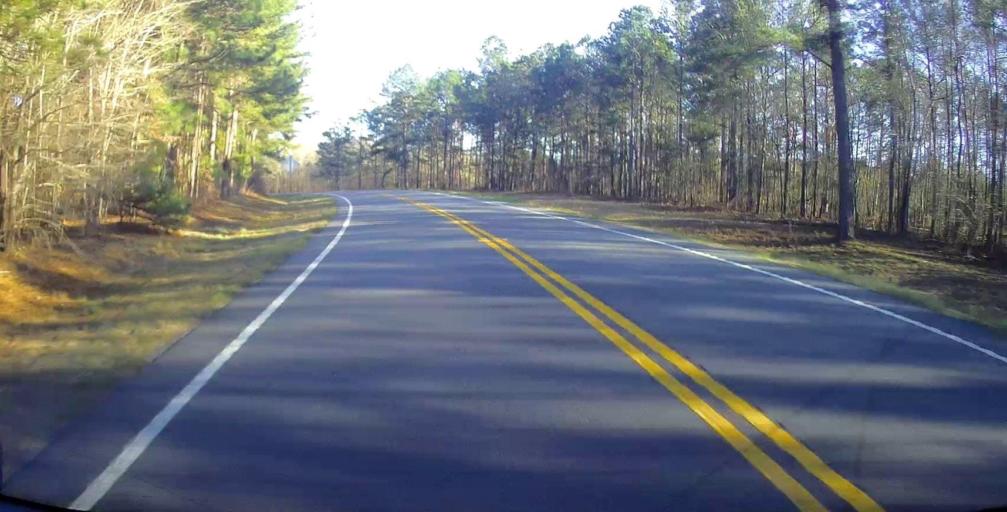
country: US
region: Georgia
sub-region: Taylor County
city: Butler
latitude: 32.4827
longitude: -84.3970
